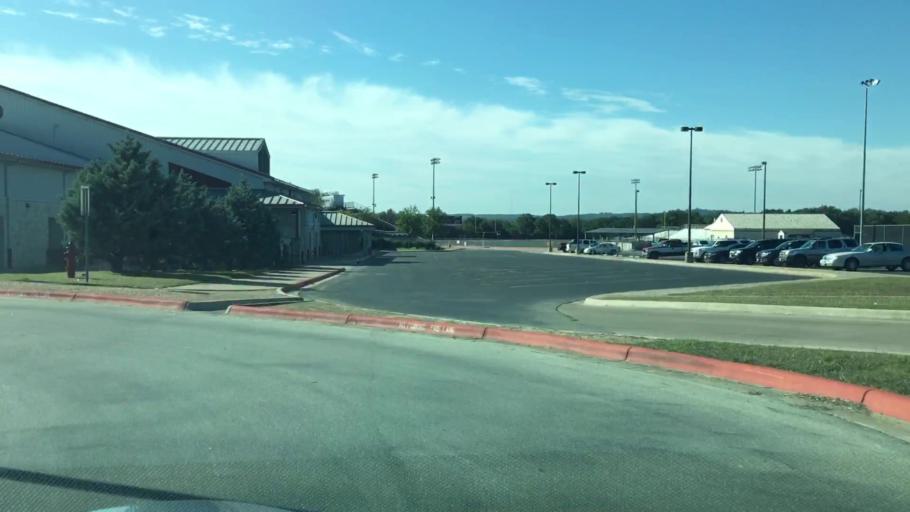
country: US
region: Texas
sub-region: Hays County
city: Dripping Springs
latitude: 30.2033
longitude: -98.1163
